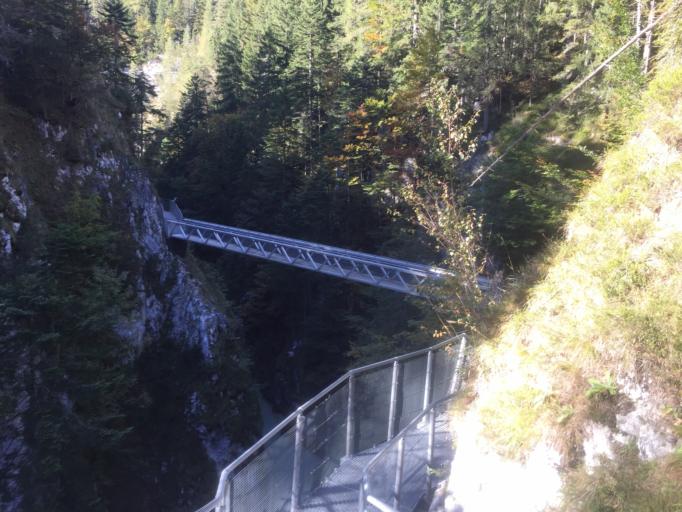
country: DE
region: Bavaria
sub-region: Upper Bavaria
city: Mittenwald
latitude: 47.4283
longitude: 11.2455
